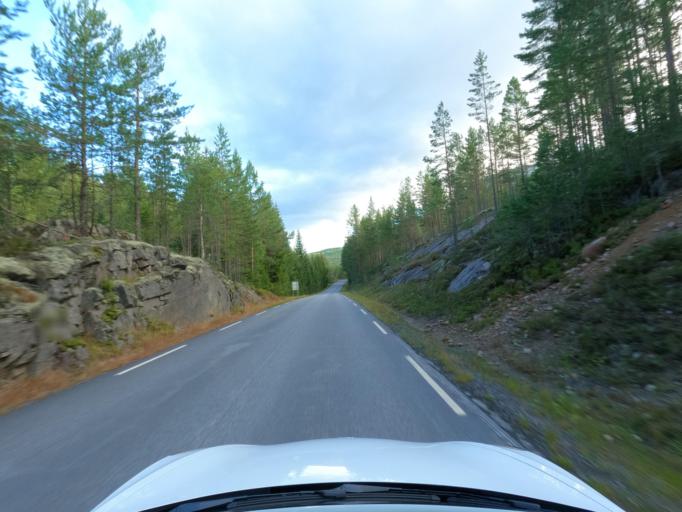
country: NO
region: Telemark
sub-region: Hjartdal
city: Sauland
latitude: 59.7801
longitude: 9.0980
